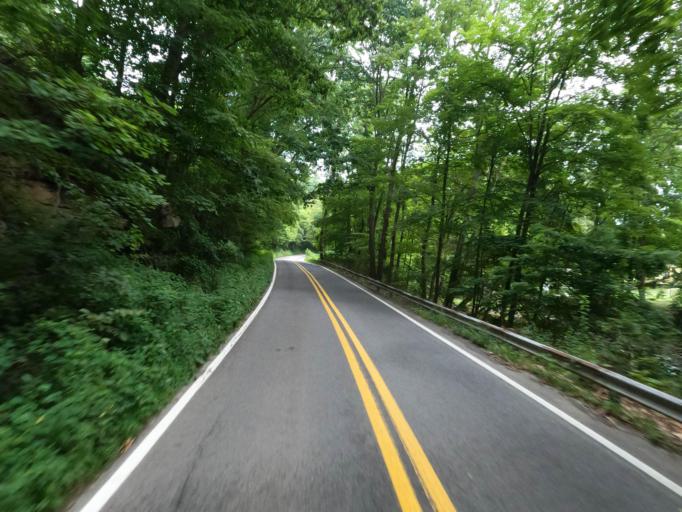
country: US
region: West Virginia
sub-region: Marion County
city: Fairmont
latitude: 39.4993
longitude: -80.0954
